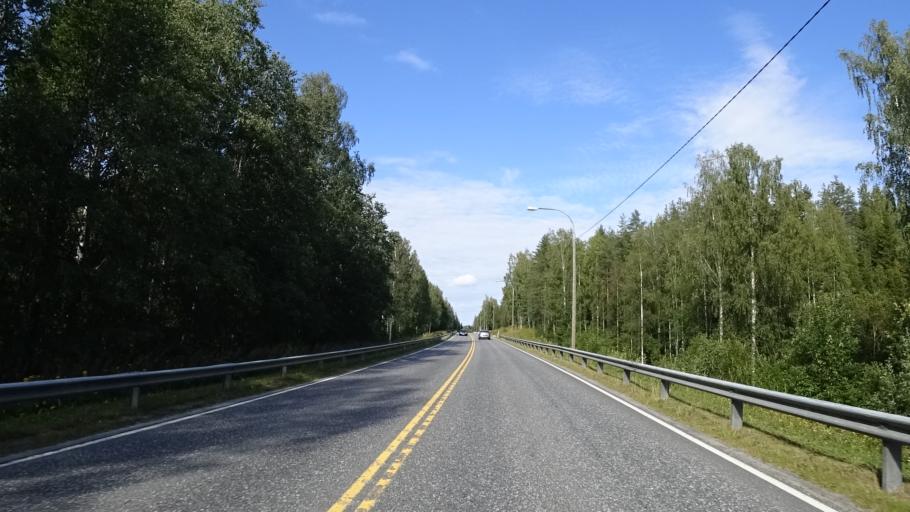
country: FI
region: North Karelia
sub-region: Joensuu
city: Eno
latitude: 62.7852
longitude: 30.0786
